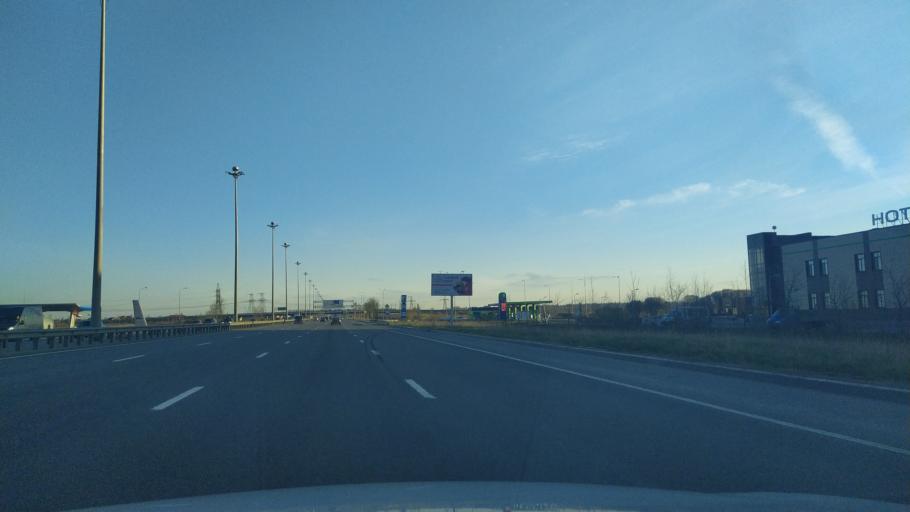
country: RU
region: St.-Petersburg
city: Aleksandrovskaya
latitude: 59.7510
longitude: 30.3163
